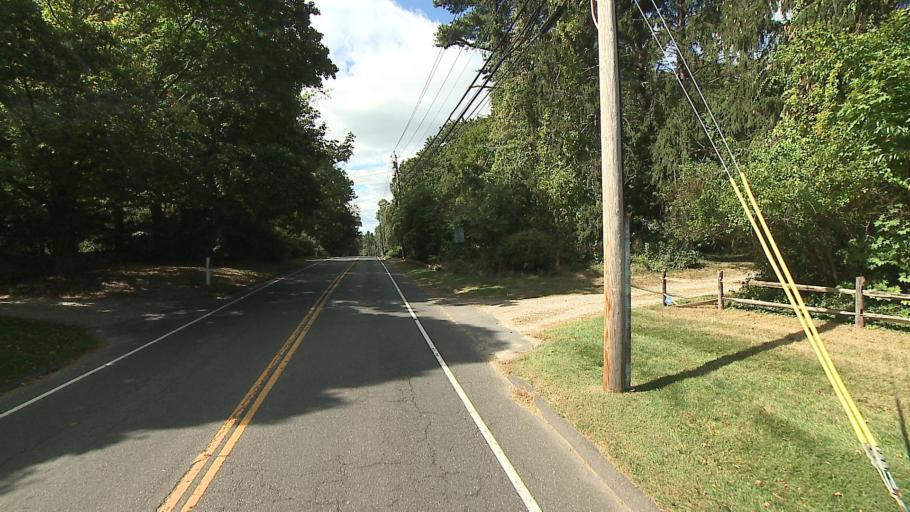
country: US
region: Connecticut
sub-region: Fairfield County
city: Wilton
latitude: 41.1753
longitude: -73.4402
